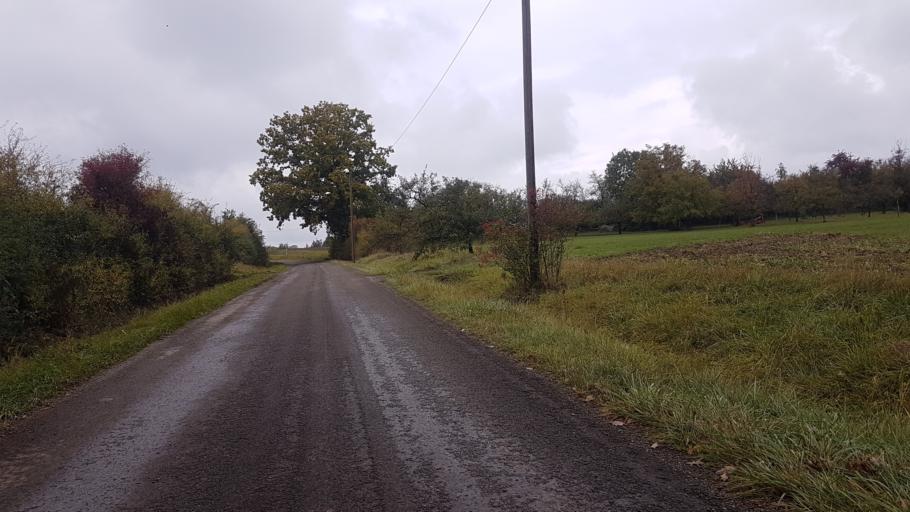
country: DE
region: Baden-Wuerttemberg
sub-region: Tuebingen Region
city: Dusslingen
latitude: 48.4596
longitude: 9.0478
